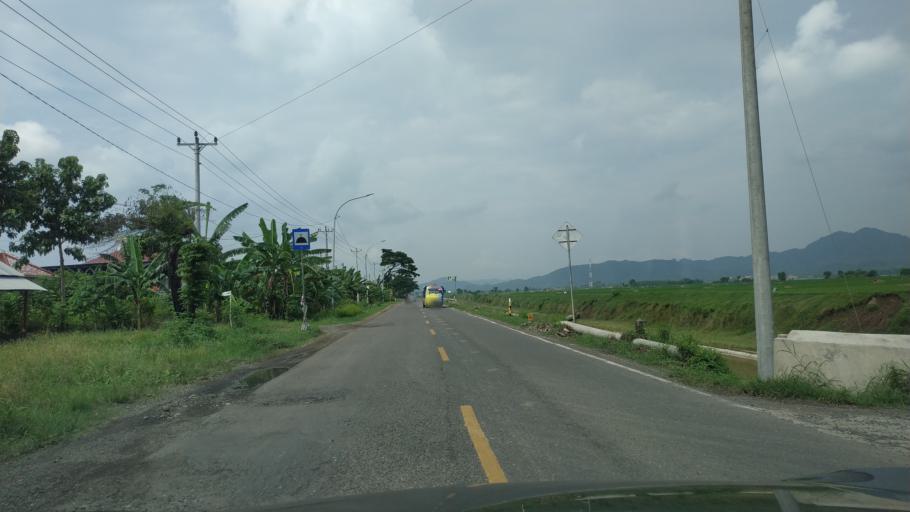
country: ID
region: Central Java
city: Margasari
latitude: -7.0761
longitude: 108.9828
